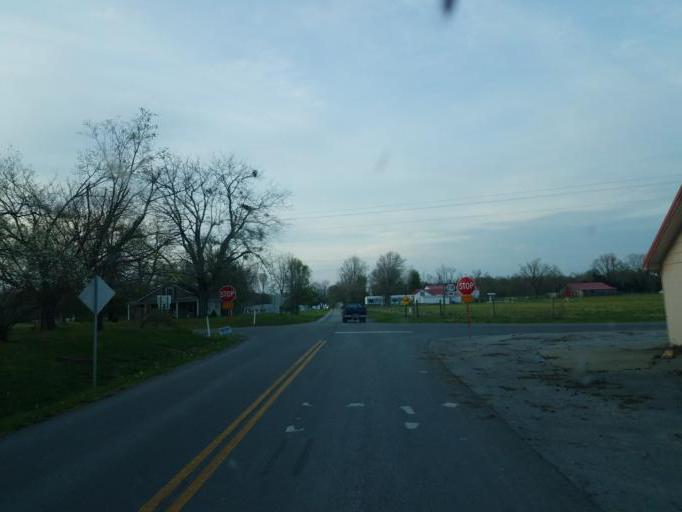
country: US
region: Kentucky
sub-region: Metcalfe County
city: Edmonton
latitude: 37.1640
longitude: -85.6829
